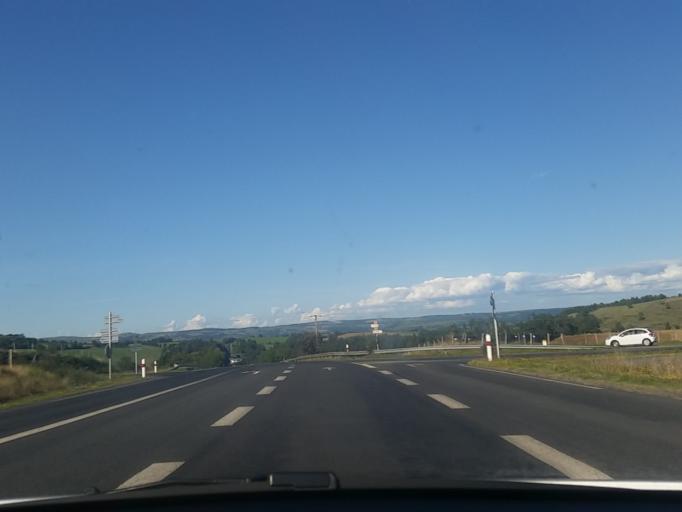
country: FR
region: Auvergne
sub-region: Departement du Cantal
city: Saint-Flour
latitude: 45.0059
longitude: 3.0430
